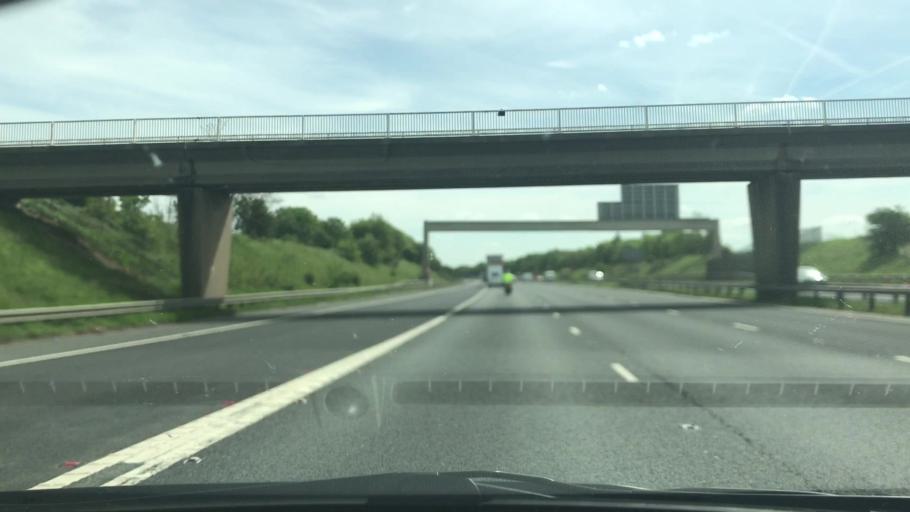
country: GB
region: England
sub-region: City and Borough of Wakefield
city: Knottingley
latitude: 53.6939
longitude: -1.2578
